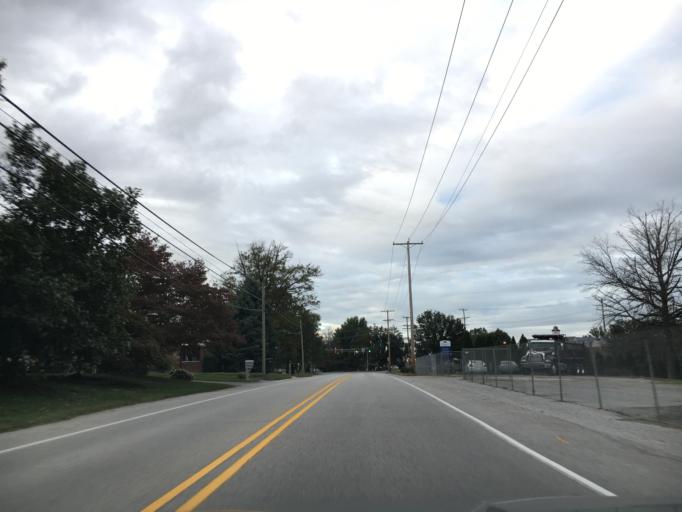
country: US
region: Pennsylvania
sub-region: York County
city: Grantley
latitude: 39.9251
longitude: -76.7145
